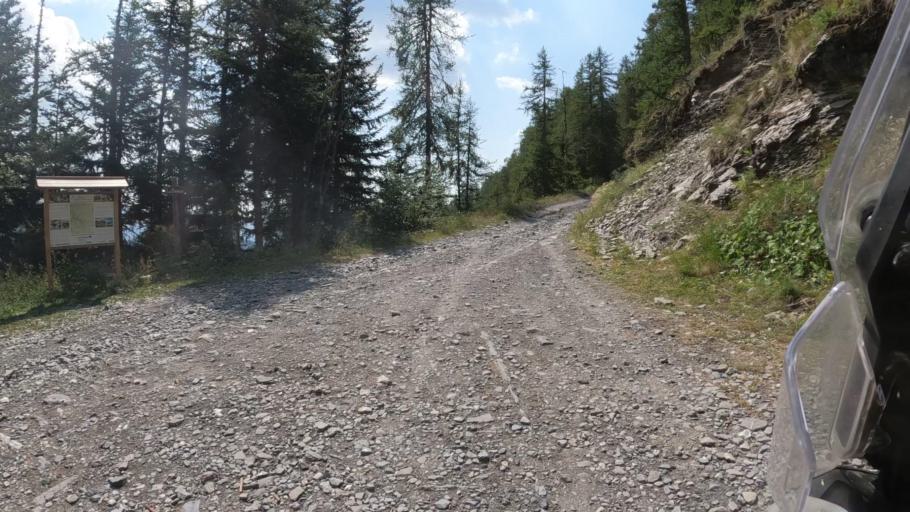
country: IT
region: Piedmont
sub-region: Provincia di Cuneo
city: Briga Alta
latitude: 44.0459
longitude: 7.7033
